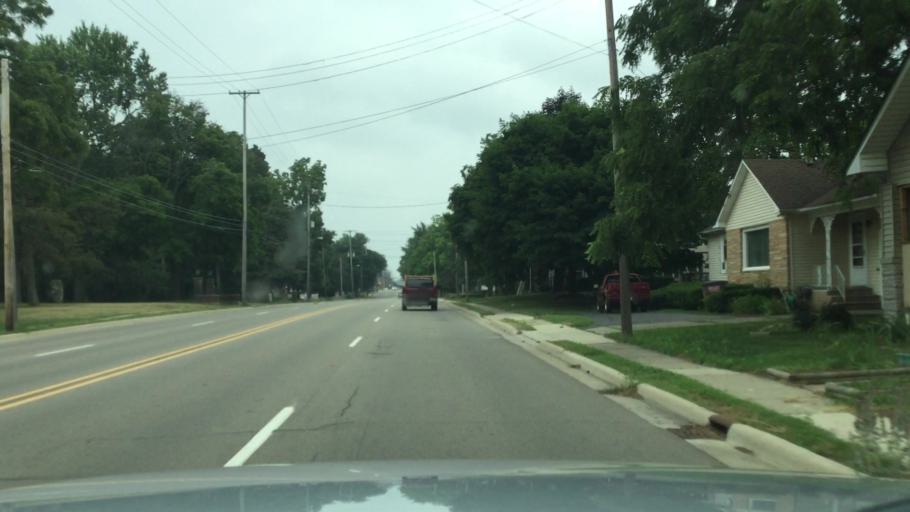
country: US
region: Michigan
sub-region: Shiawassee County
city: Owosso
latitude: 43.0095
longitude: -84.1768
